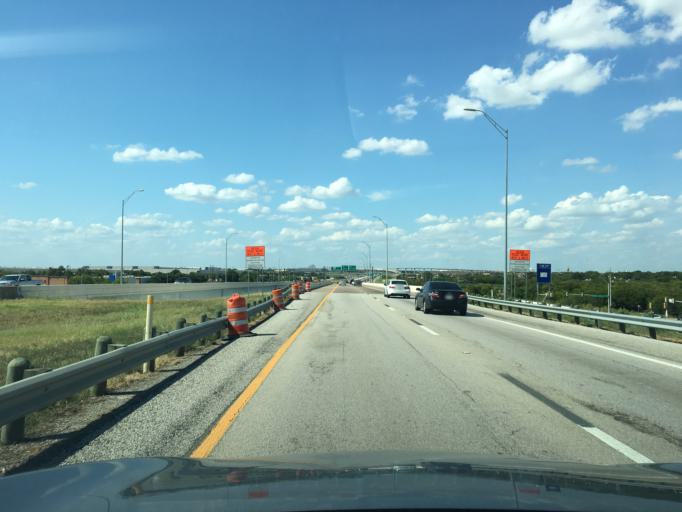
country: US
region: Texas
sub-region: Tarrant County
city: Arlington
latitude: 32.6601
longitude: -97.0622
